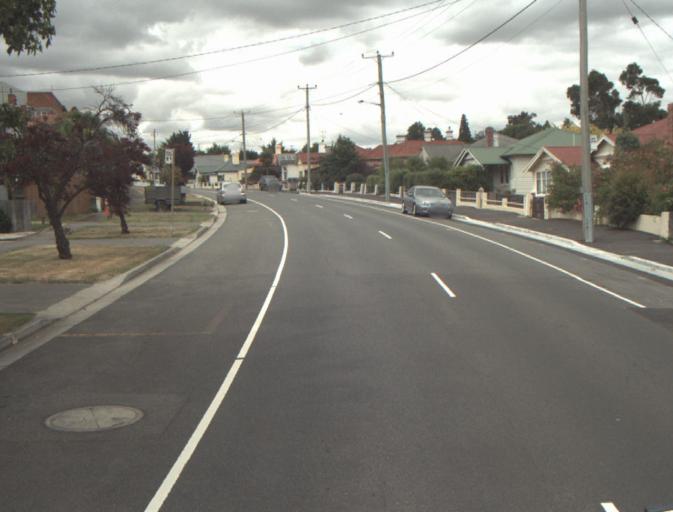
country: AU
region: Tasmania
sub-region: Launceston
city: East Launceston
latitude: -41.4567
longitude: 147.1509
